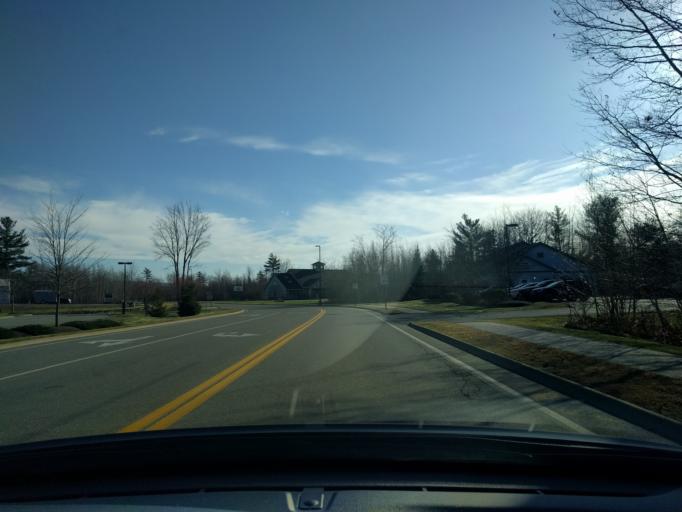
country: US
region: Maine
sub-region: Penobscot County
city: Brewer
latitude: 44.7813
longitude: -68.7534
